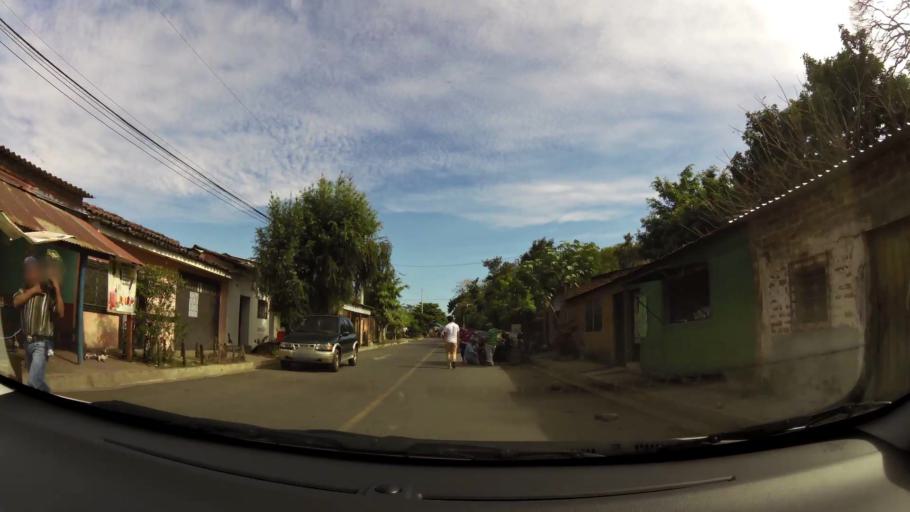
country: SV
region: Santa Ana
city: Chalchuapa
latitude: 13.9813
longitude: -89.6758
